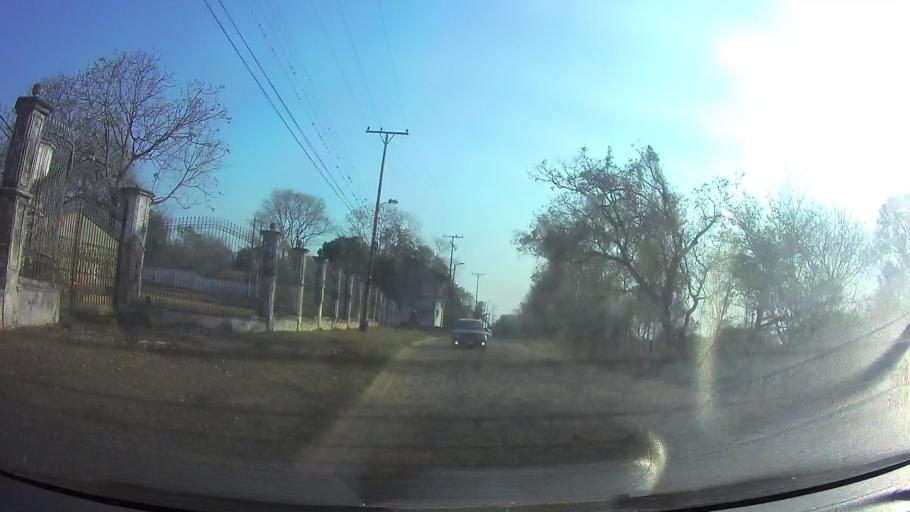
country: PY
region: Central
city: Limpio
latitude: -25.2213
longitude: -57.5045
